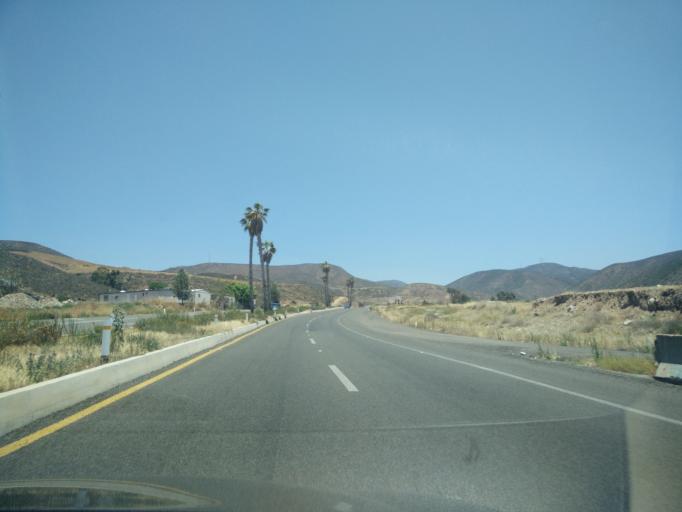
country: MX
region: Baja California
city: El Sauzal
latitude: 31.9209
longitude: -116.6818
